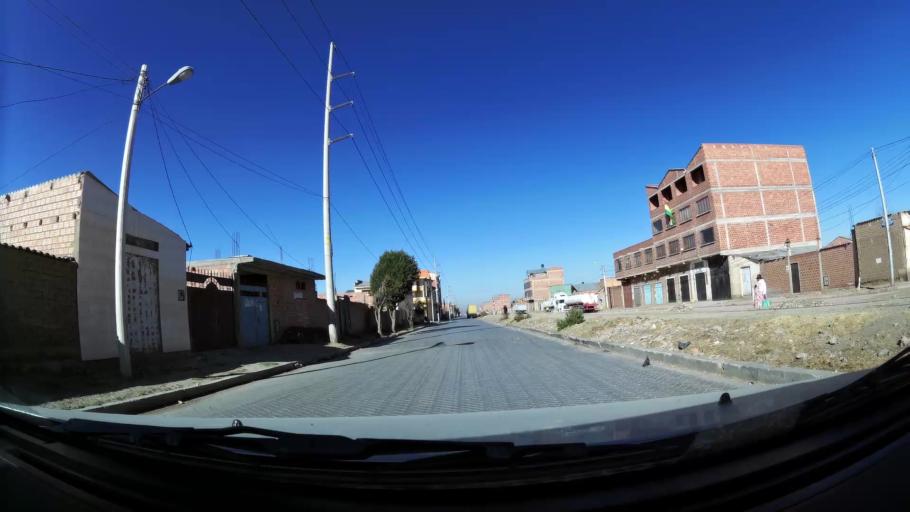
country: BO
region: La Paz
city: La Paz
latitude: -16.5320
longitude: -68.1674
